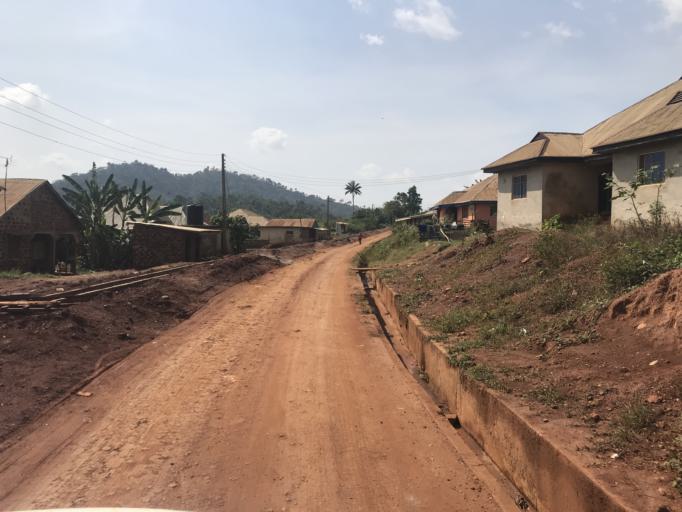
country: NG
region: Osun
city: Ilesa
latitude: 7.6212
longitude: 4.7011
